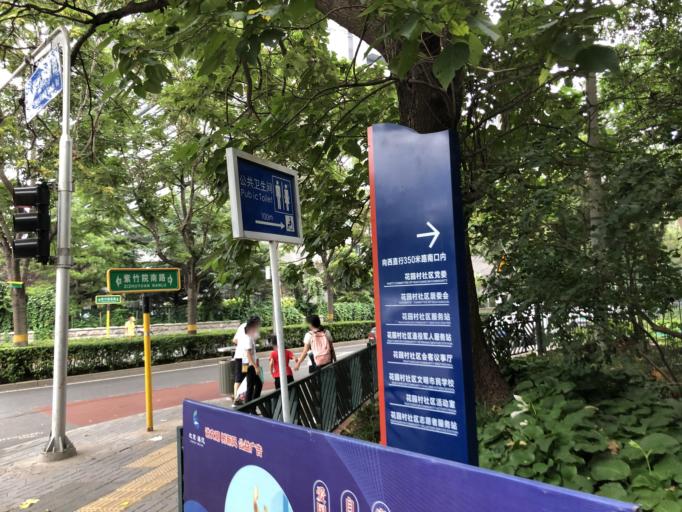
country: CN
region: Beijing
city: Jinrongjie
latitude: 39.9309
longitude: 116.3135
